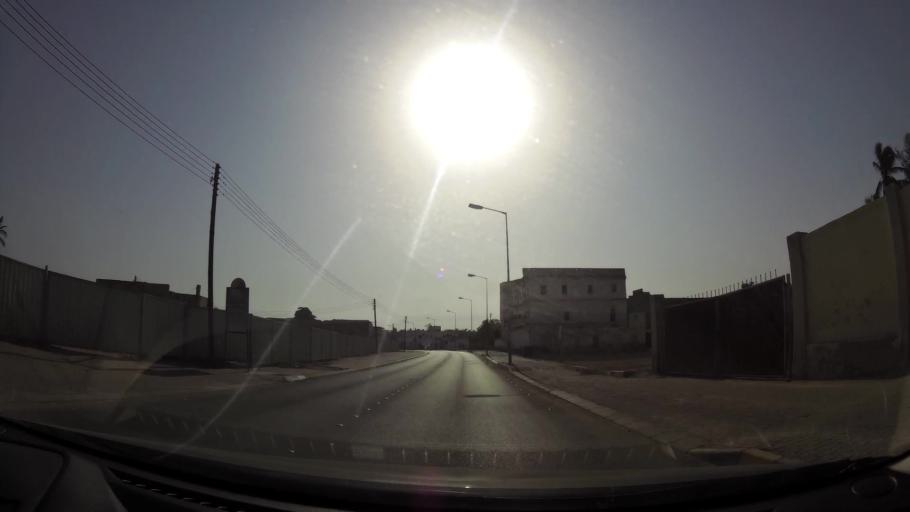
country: OM
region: Zufar
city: Salalah
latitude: 17.0034
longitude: 54.1086
